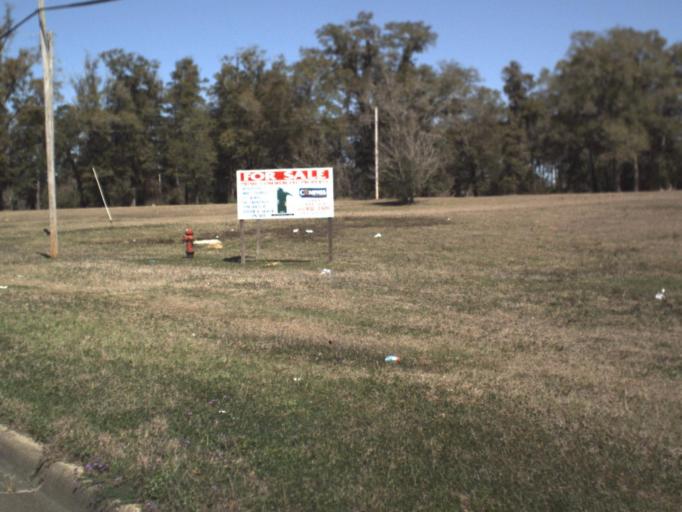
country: US
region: Florida
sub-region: Jackson County
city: Marianna
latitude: 30.7603
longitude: -85.1979
